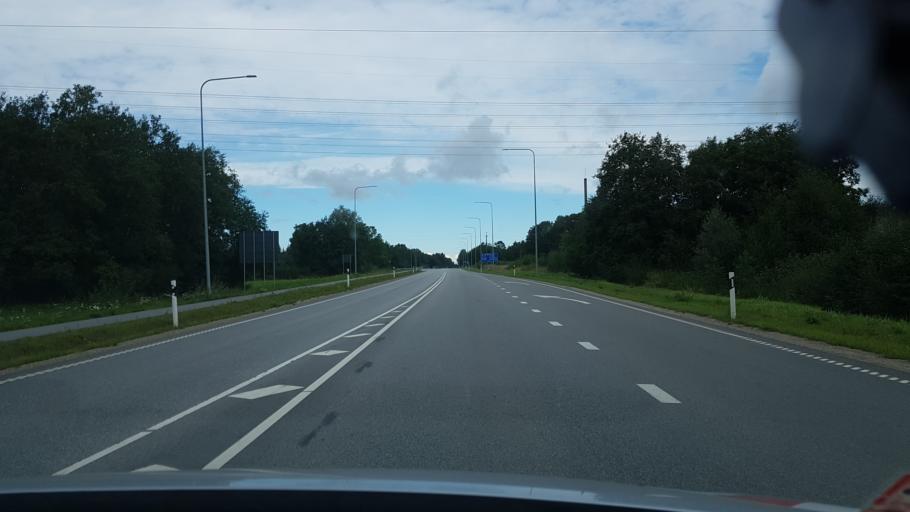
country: EE
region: Viljandimaa
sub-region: Viljandi linn
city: Viljandi
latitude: 58.3739
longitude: 25.5637
